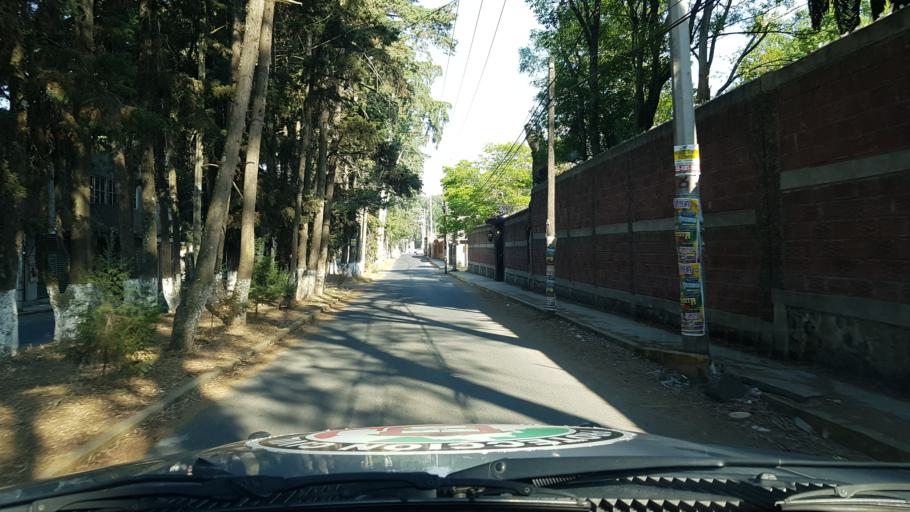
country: MX
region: Mexico
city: Ozumba de Alzate
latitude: 19.0623
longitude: -98.7829
